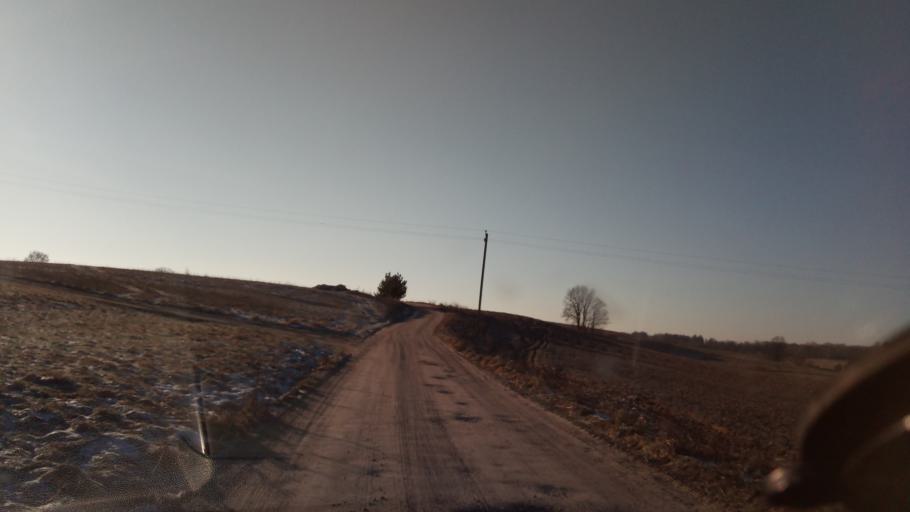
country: LT
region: Alytaus apskritis
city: Druskininkai
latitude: 54.1128
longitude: 24.0137
